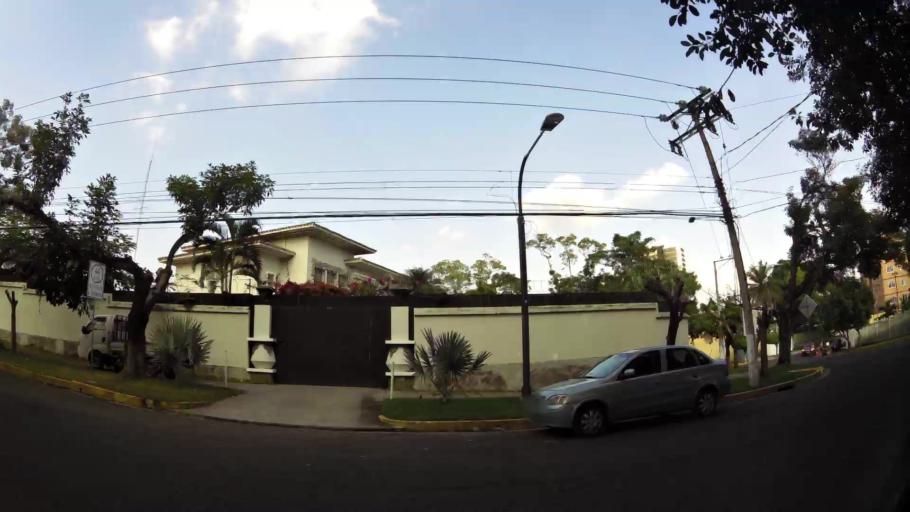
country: SV
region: La Libertad
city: Antiguo Cuscatlan
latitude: 13.6942
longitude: -89.2398
